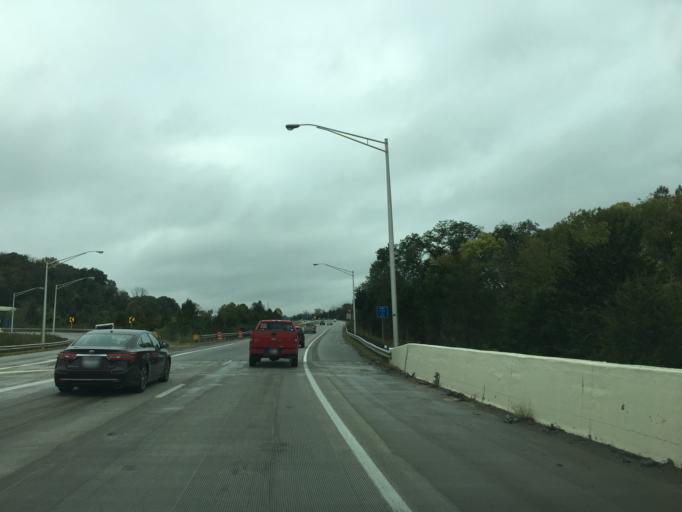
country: US
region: Ohio
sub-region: Hamilton County
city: Miamitown
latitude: 39.2154
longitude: -84.6768
